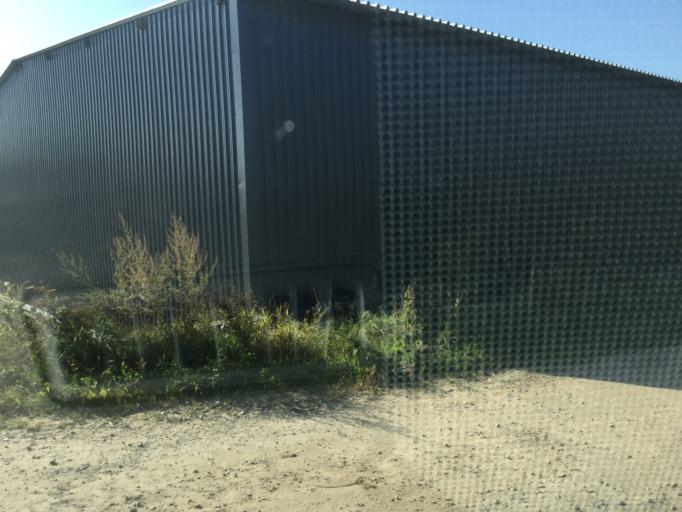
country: BY
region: Vitebsk
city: Vitebsk
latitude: 55.1817
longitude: 30.2548
